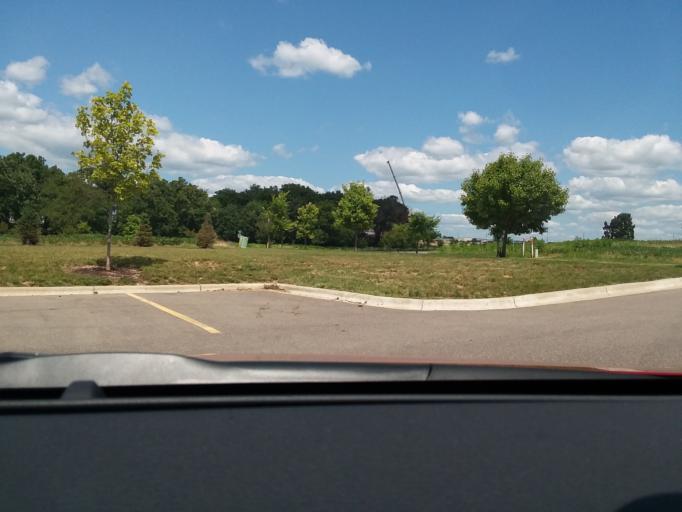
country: US
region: Wisconsin
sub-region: Dane County
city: Windsor
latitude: 43.2000
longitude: -89.3297
